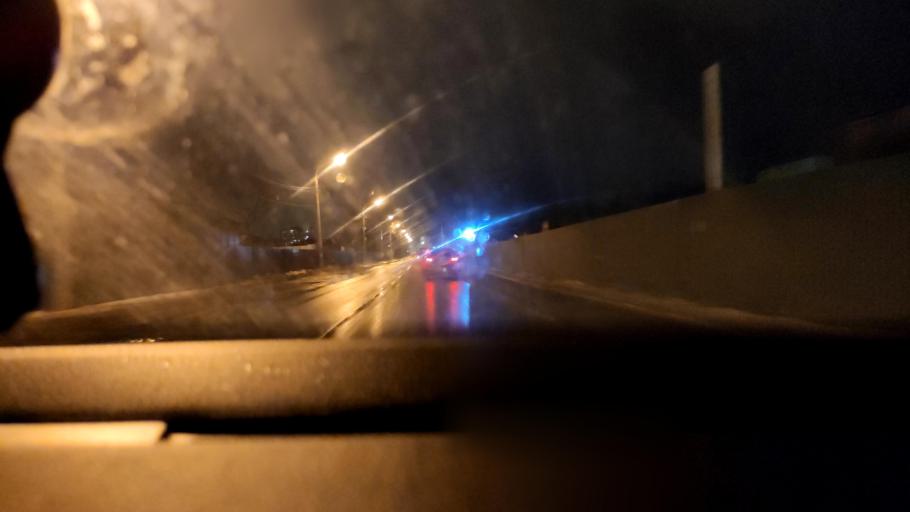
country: RU
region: Moskovskaya
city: Zhukovskiy
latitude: 55.5861
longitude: 38.1056
